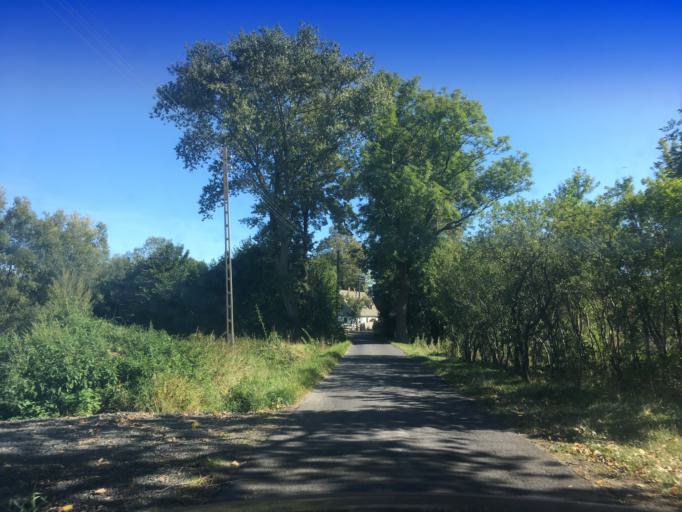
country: PL
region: Lower Silesian Voivodeship
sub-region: Powiat lubanski
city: Swieradow-Zdroj
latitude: 50.9583
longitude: 15.3159
